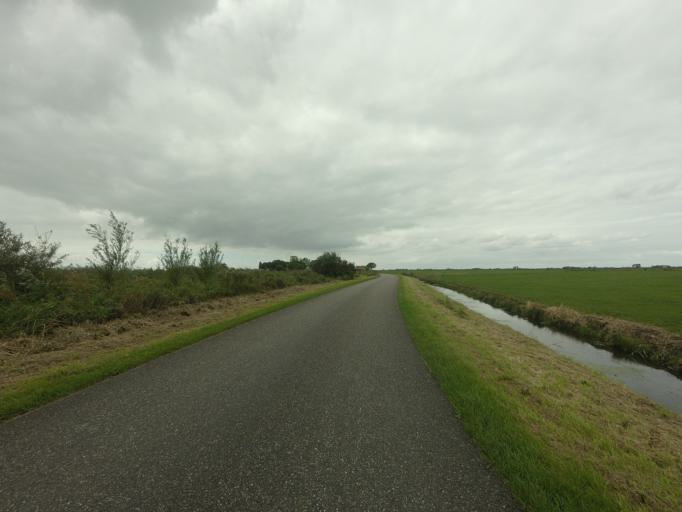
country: NL
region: Friesland
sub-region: Sudwest Fryslan
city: Bolsward
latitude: 52.9867
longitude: 5.5264
